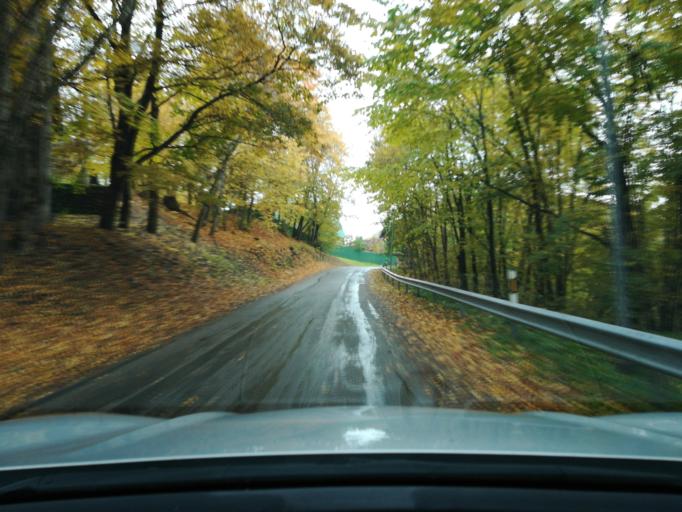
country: EE
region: Ida-Virumaa
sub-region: Johvi vald
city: Johvi
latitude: 59.1997
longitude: 27.5367
